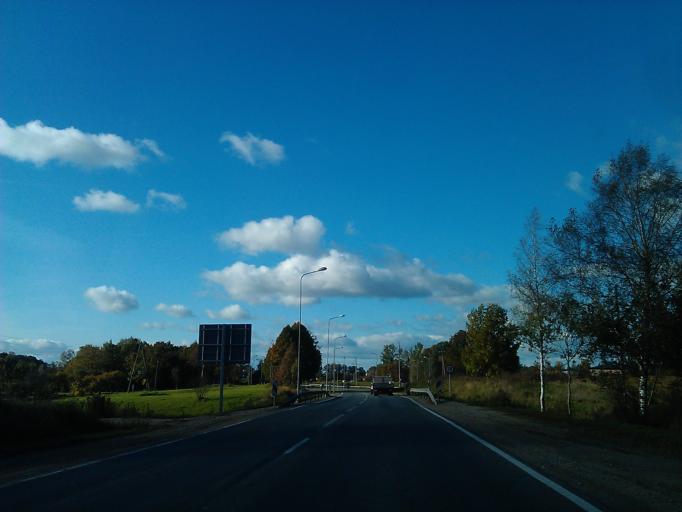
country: LV
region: Koknese
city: Koknese
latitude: 56.6399
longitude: 25.4486
